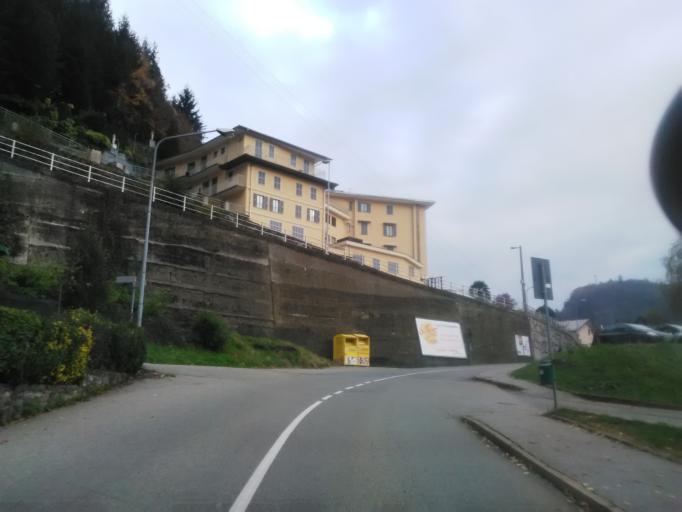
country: IT
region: Piedmont
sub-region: Provincia di Vercelli
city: Varallo
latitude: 45.8189
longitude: 8.2533
